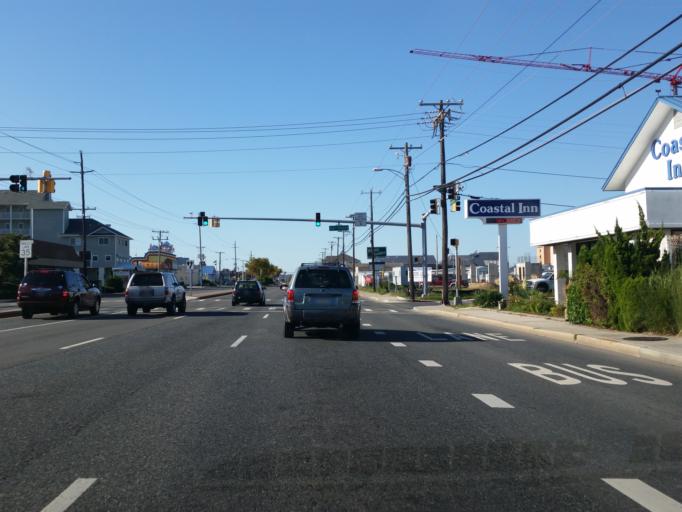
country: US
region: Maryland
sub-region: Worcester County
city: Ocean City
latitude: 38.3557
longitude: -75.0757
